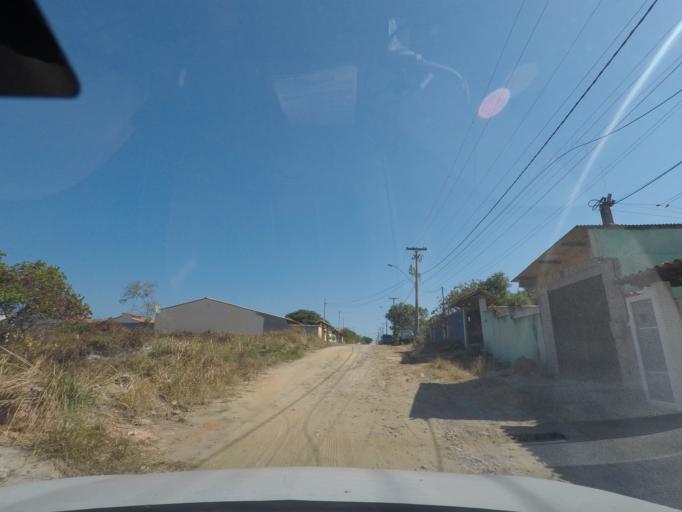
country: BR
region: Rio de Janeiro
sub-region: Marica
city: Marica
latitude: -22.9653
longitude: -42.9083
